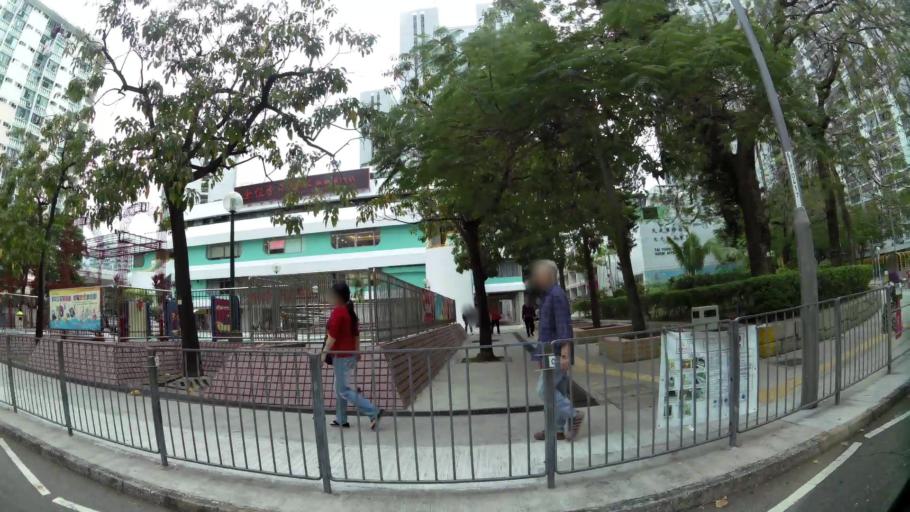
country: HK
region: Tai Po
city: Tai Po
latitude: 22.4553
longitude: 114.1693
